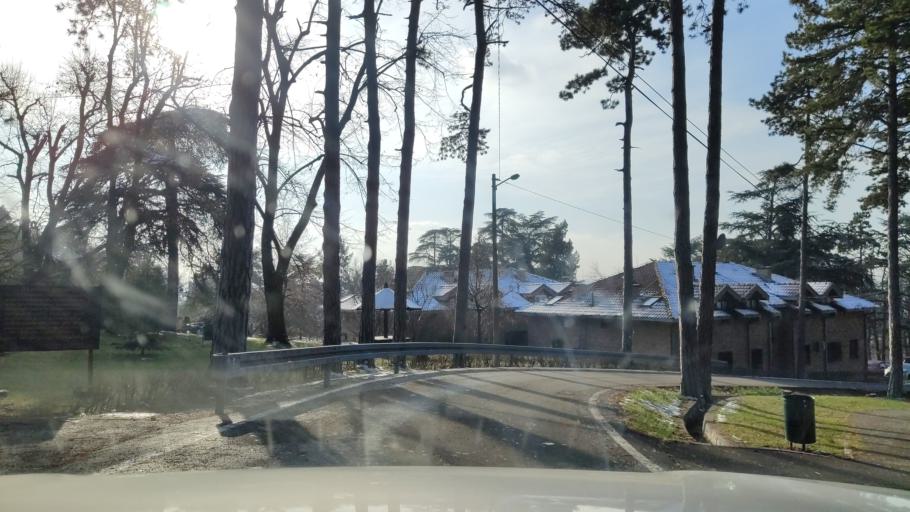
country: RS
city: Rusanj
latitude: 44.6958
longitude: 20.5043
